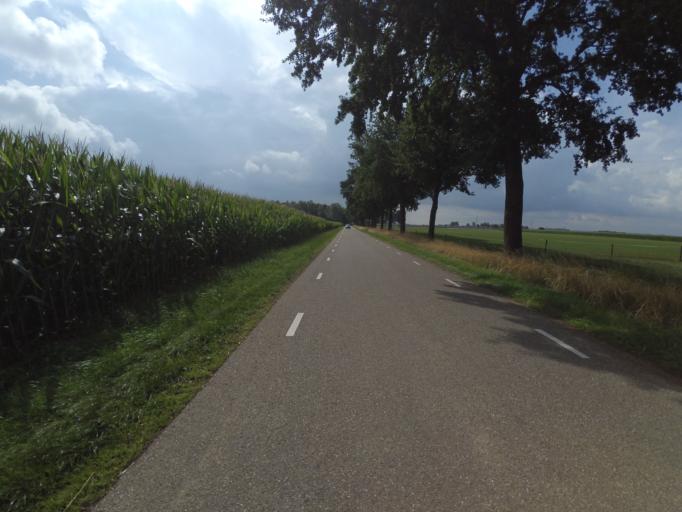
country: NL
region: Limburg
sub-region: Gemeente Echt-Susteren
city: Koningsbosch
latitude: 51.0458
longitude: 5.9487
